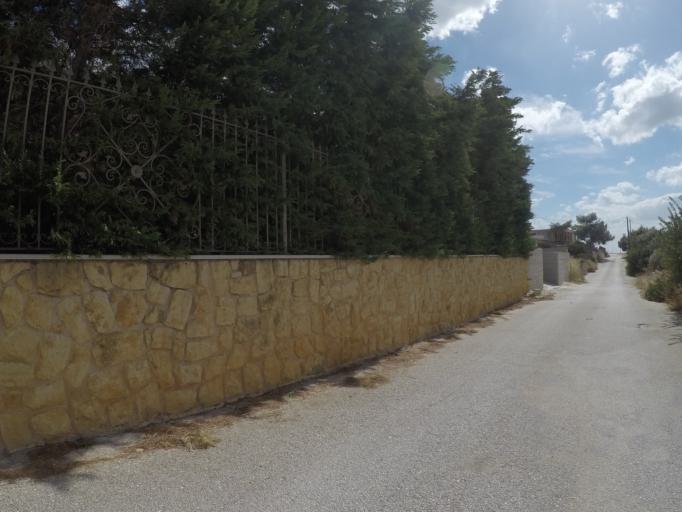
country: GR
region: Attica
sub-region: Nomarchia Anatolikis Attikis
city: Agios Dimitrios Kropias
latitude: 37.8018
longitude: 23.8785
